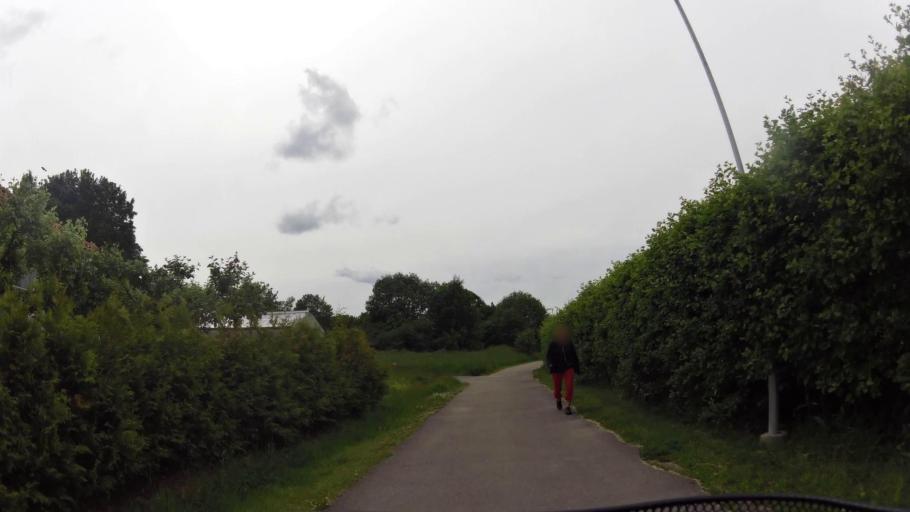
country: SE
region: OEstergoetland
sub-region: Linkopings Kommun
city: Linkoping
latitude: 58.3864
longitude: 15.5758
